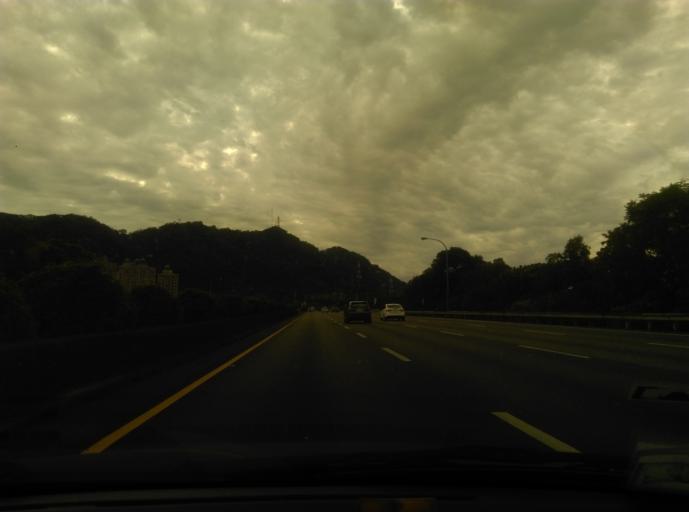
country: TW
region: Taiwan
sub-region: Taoyuan
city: Taoyuan
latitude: 24.9427
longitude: 121.3640
